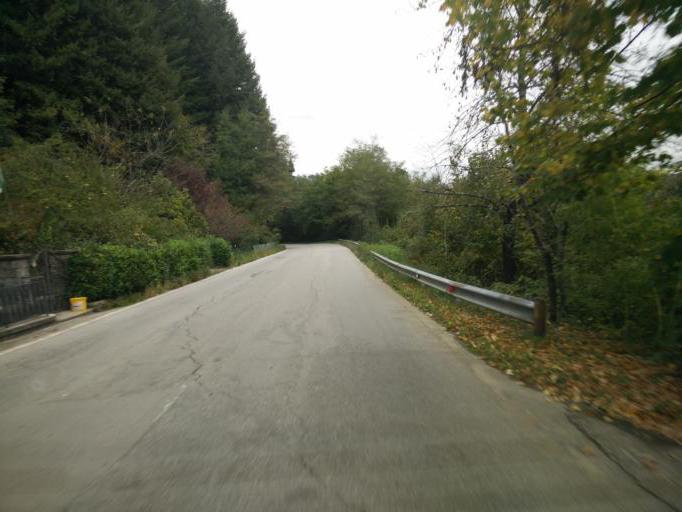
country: IT
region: Tuscany
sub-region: Provincia di Lucca
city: Camporgiano
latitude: 44.1729
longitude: 10.3216
